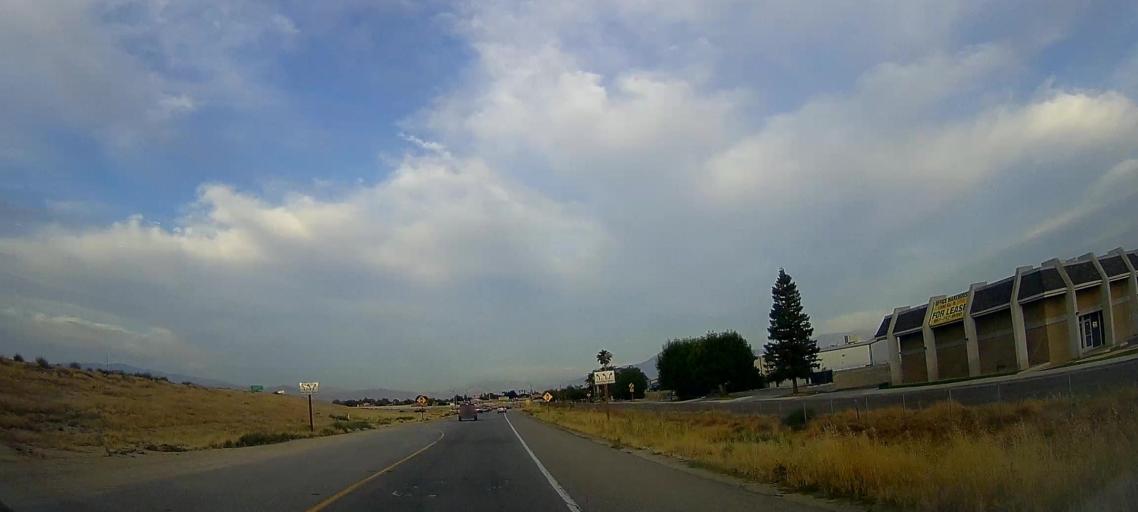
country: US
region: California
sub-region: Kern County
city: Bakersfield
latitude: 35.3518
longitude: -118.9527
